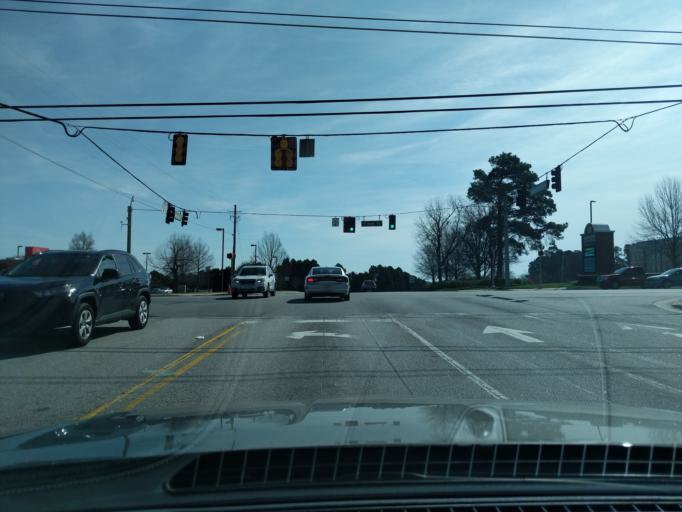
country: US
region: Georgia
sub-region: Columbia County
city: Evans
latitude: 33.5336
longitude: -82.1307
